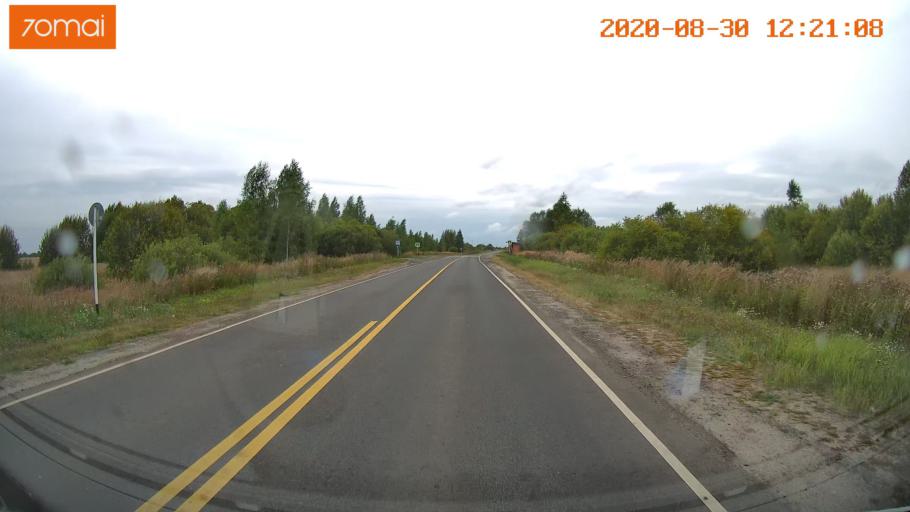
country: RU
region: Ivanovo
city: Yur'yevets
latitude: 57.3240
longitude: 42.8828
